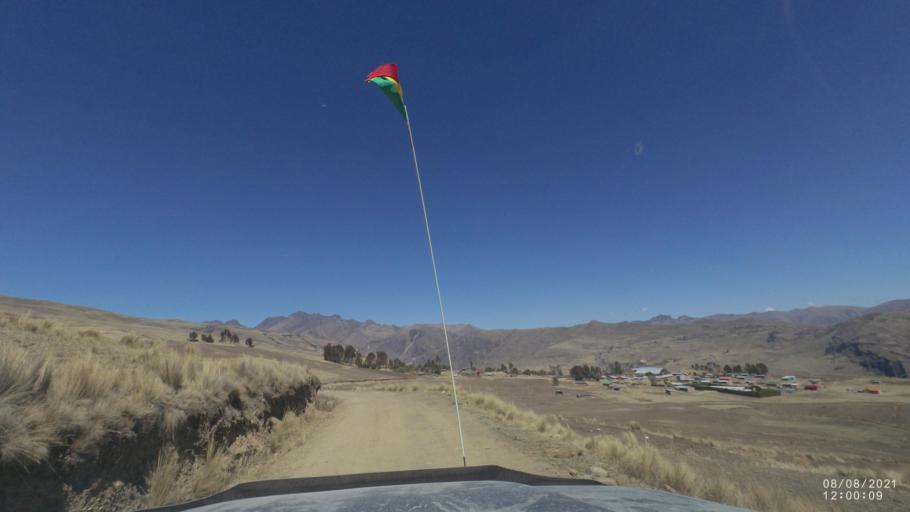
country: BO
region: Cochabamba
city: Colchani
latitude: -16.8354
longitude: -66.6265
